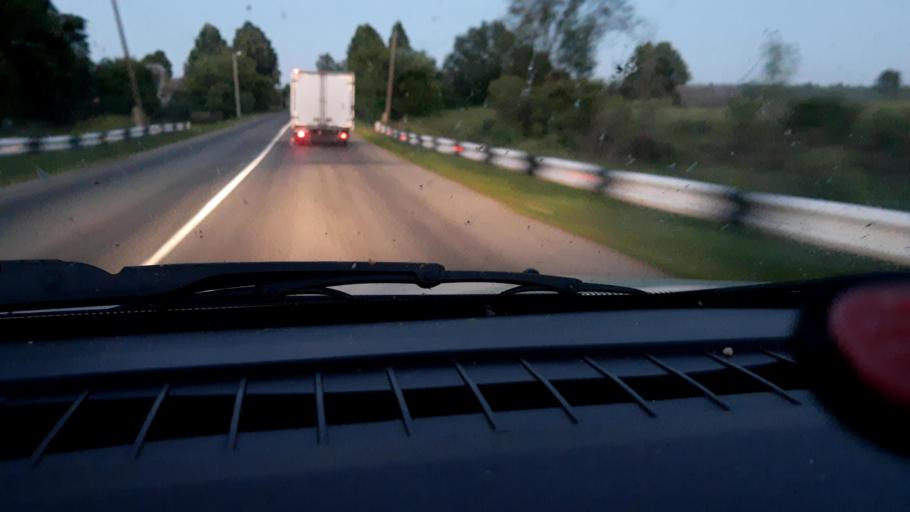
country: RU
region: Nizjnij Novgorod
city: Tonkino
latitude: 57.3732
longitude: 46.3713
